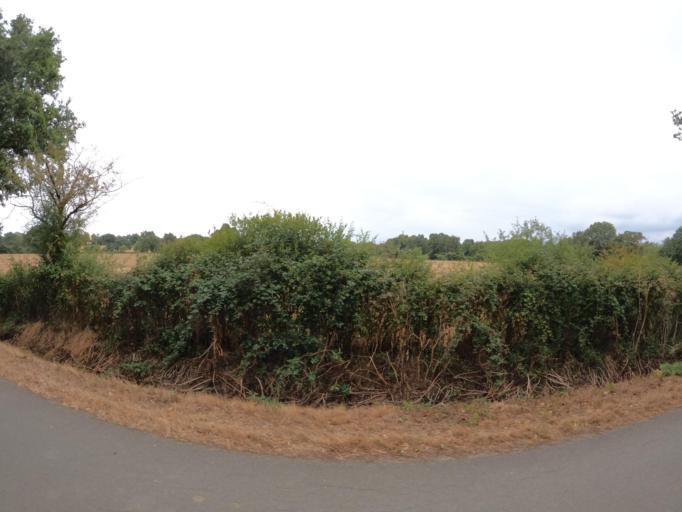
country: FR
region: Pays de la Loire
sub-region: Departement de Maine-et-Loire
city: La Romagne
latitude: 47.0482
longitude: -0.9955
